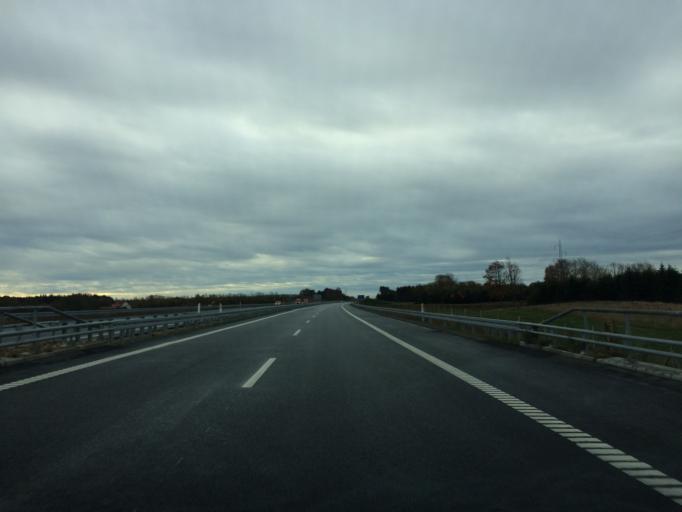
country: DK
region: Central Jutland
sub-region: Silkeborg Kommune
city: Silkeborg
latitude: 56.1638
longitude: 9.4682
